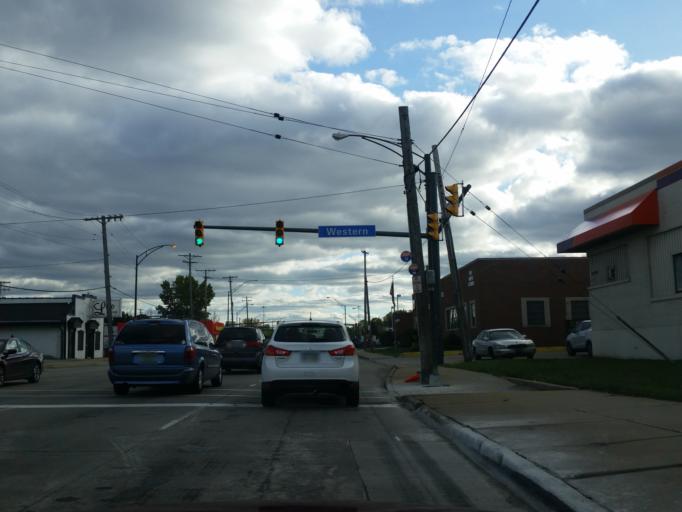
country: US
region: Ohio
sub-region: Cuyahoga County
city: Lakewood
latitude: 41.4706
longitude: -81.7689
